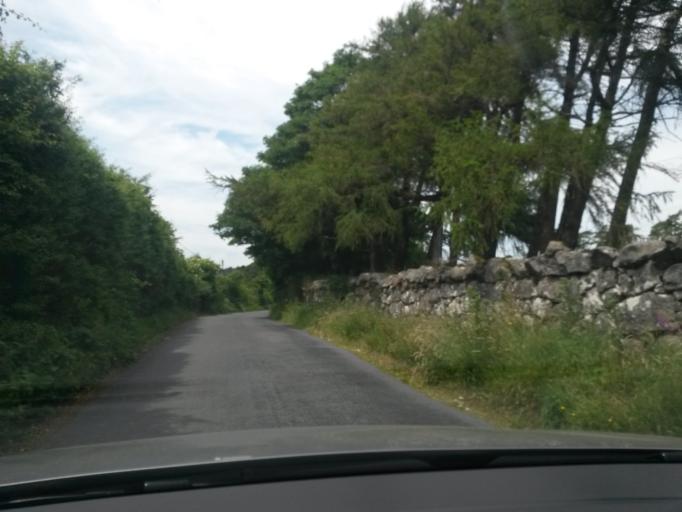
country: IE
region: Leinster
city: Ballinteer
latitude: 53.1959
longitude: -6.2833
